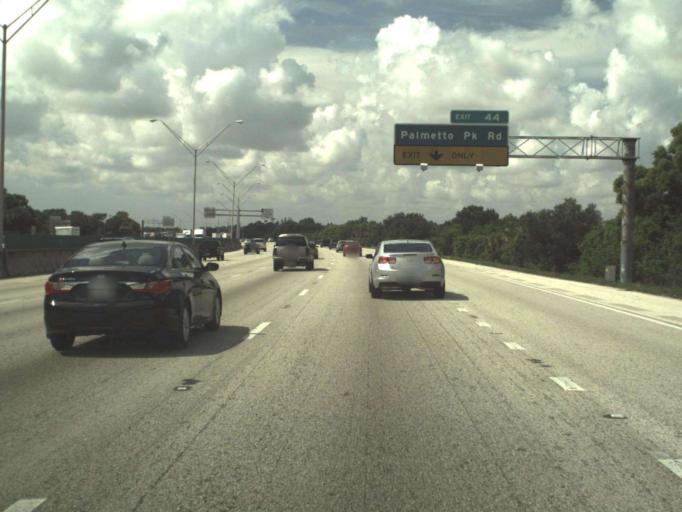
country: US
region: Florida
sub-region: Palm Beach County
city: Boca Del Mar
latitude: 26.3616
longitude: -80.1201
